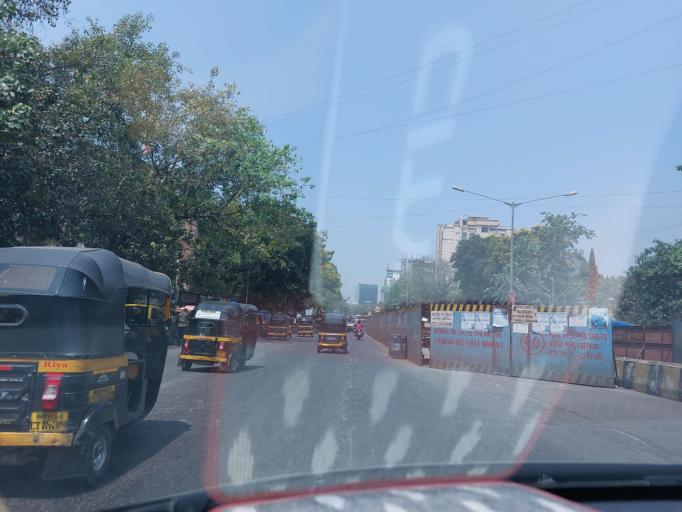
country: IN
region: Maharashtra
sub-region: Mumbai Suburban
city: Mumbai
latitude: 19.0541
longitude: 72.8942
